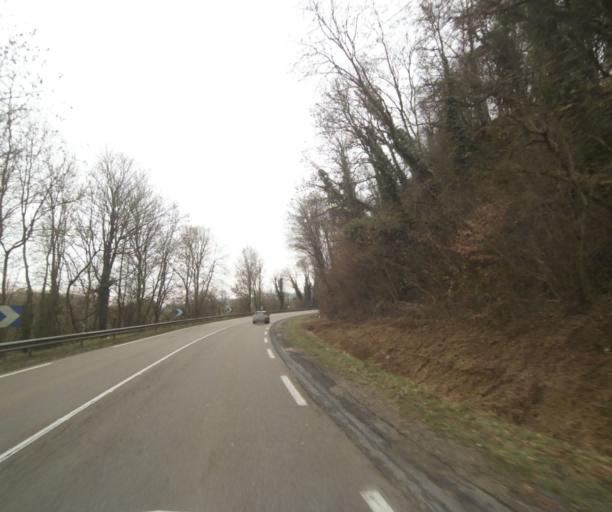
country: FR
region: Champagne-Ardenne
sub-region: Departement de la Haute-Marne
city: Bienville
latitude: 48.6008
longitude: 5.0334
